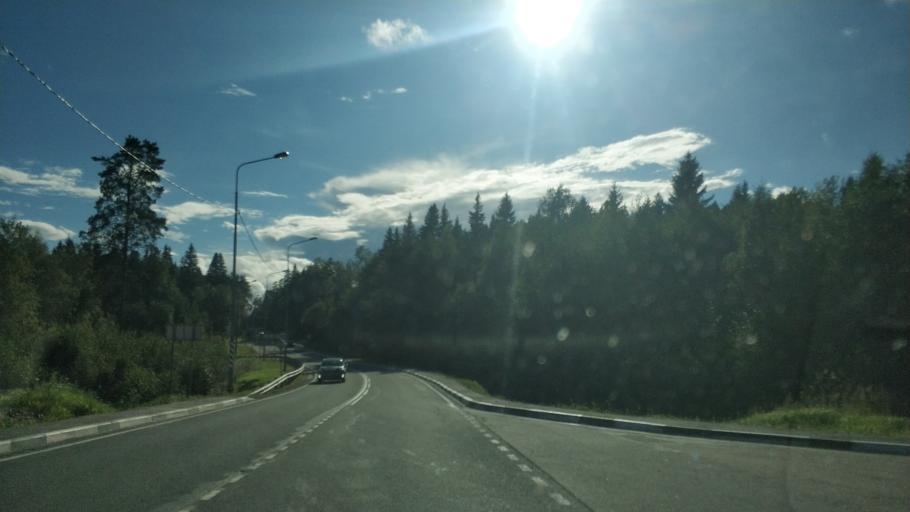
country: RU
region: Republic of Karelia
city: Lakhdenpokh'ya
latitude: 61.5352
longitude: 30.2138
